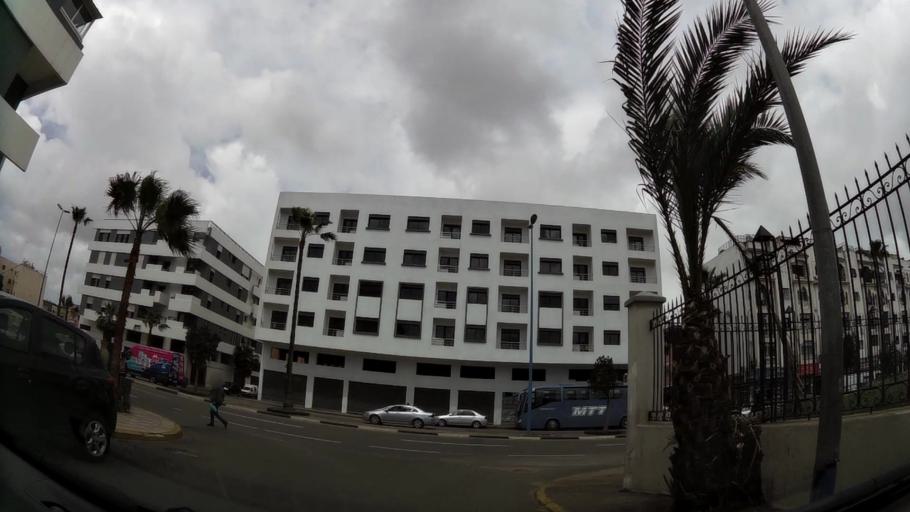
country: MA
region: Grand Casablanca
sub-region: Casablanca
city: Casablanca
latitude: 33.5436
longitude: -7.5837
